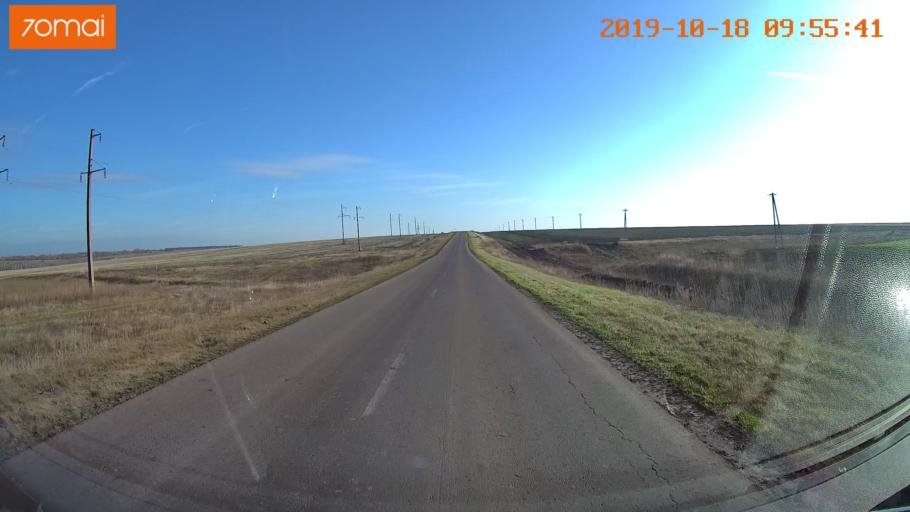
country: RU
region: Tula
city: Kurkino
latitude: 53.3710
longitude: 38.3702
